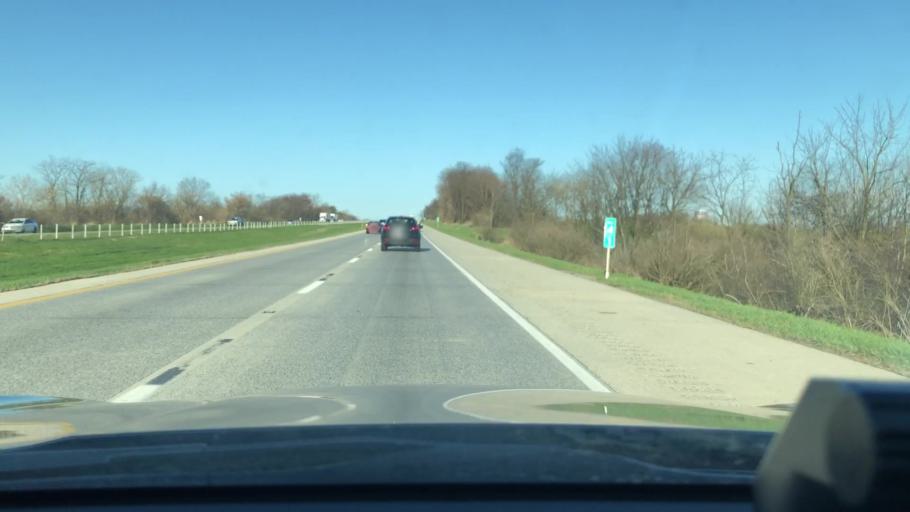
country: US
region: Pennsylvania
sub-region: Lebanon County
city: Fredericksburg
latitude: 40.4485
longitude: -76.4564
